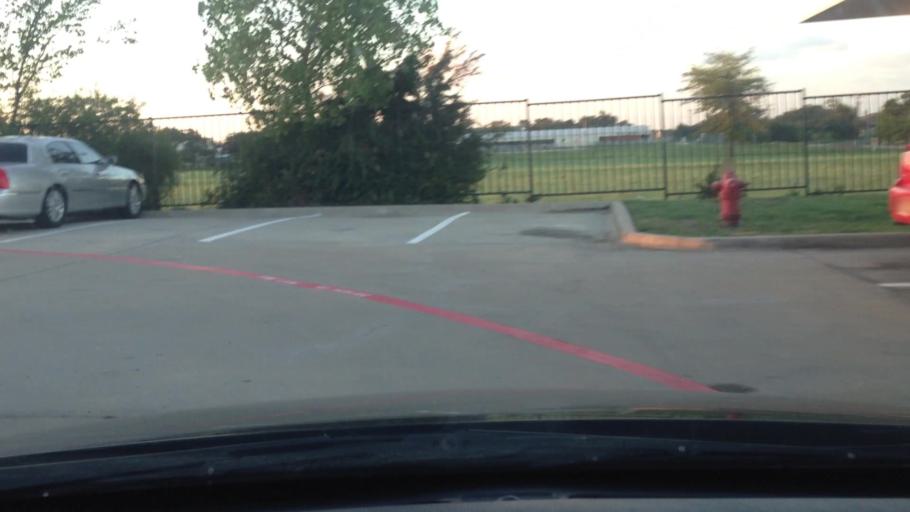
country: US
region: Texas
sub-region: Tarrant County
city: White Settlement
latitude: 32.7855
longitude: -97.4687
